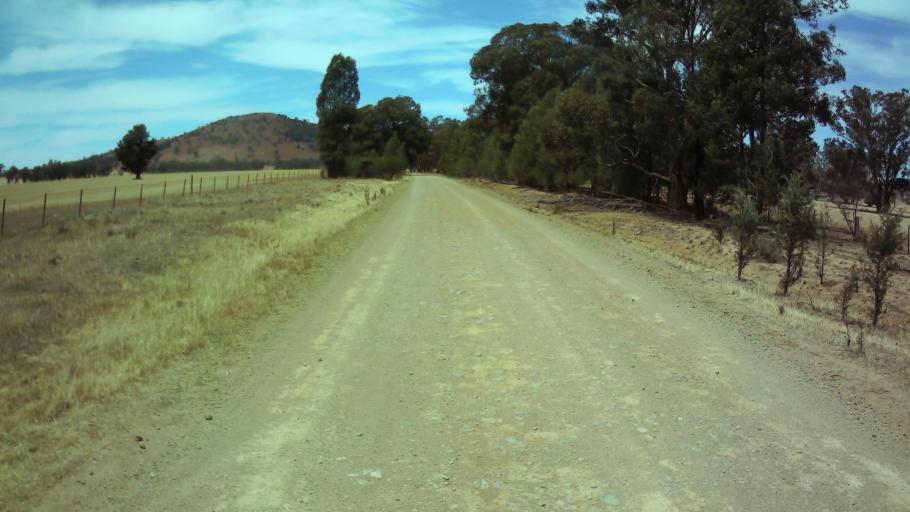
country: AU
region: New South Wales
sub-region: Weddin
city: Grenfell
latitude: -33.7623
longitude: 148.1304
